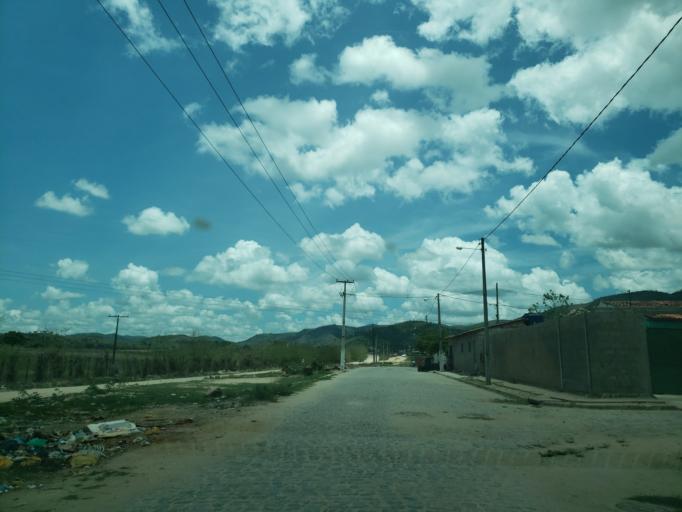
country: BR
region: Alagoas
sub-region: Uniao Dos Palmares
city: Uniao dos Palmares
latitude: -9.1488
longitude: -36.0101
